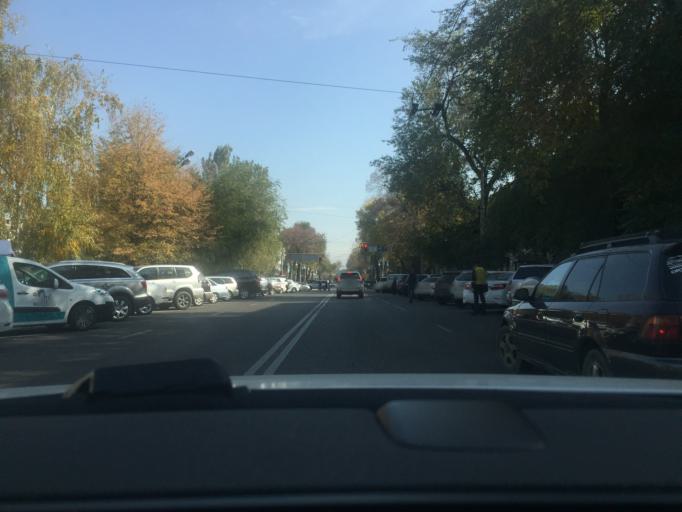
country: KZ
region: Almaty Qalasy
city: Almaty
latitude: 43.2615
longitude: 76.9375
